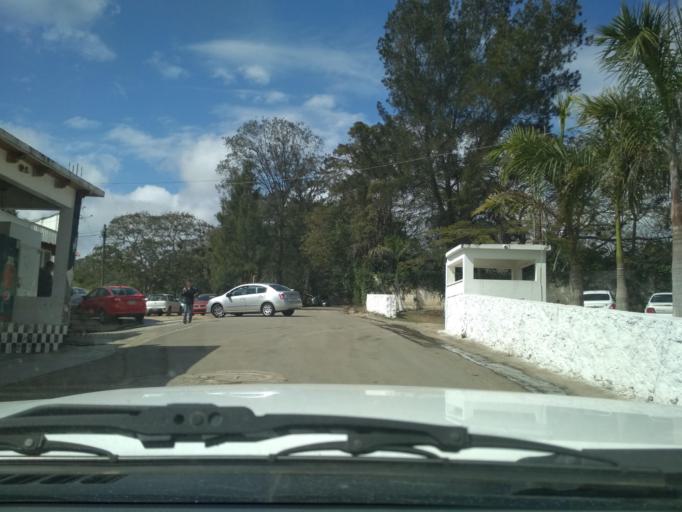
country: MX
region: Veracruz
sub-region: Emiliano Zapata
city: Dos Rios
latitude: 19.4851
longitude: -96.8133
